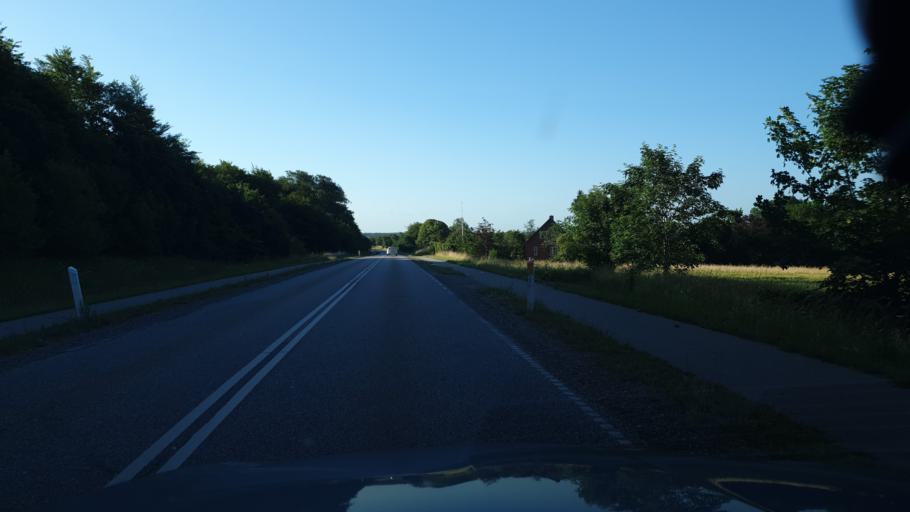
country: DK
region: Zealand
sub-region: Soro Kommune
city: Frederiksberg
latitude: 55.3976
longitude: 11.6352
